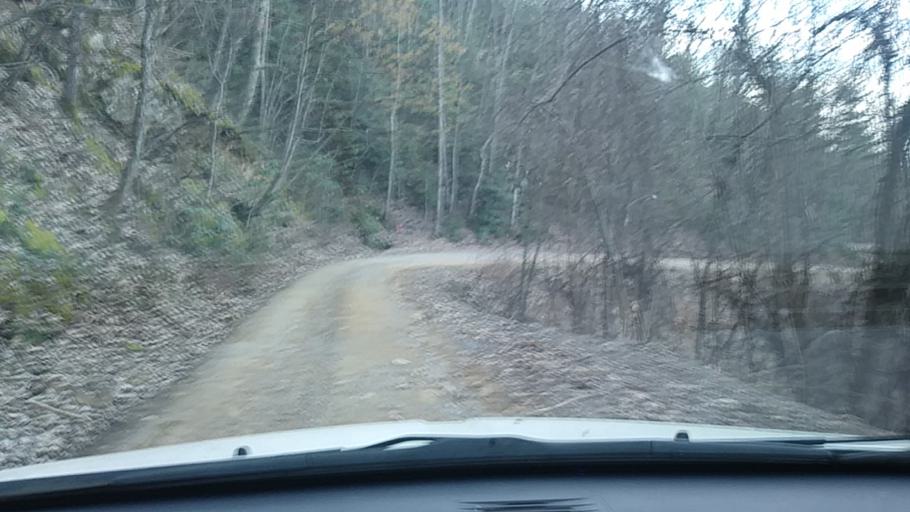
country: US
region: Tennessee
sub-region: Greene County
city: Tusculum
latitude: 36.0856
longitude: -82.6849
